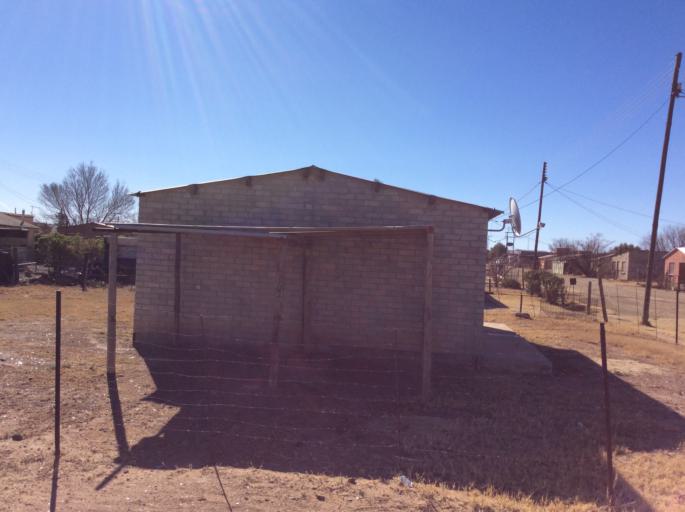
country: ZA
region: Orange Free State
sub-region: Lejweleputswa District Municipality
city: Brandfort
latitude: -28.7367
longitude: 26.1079
